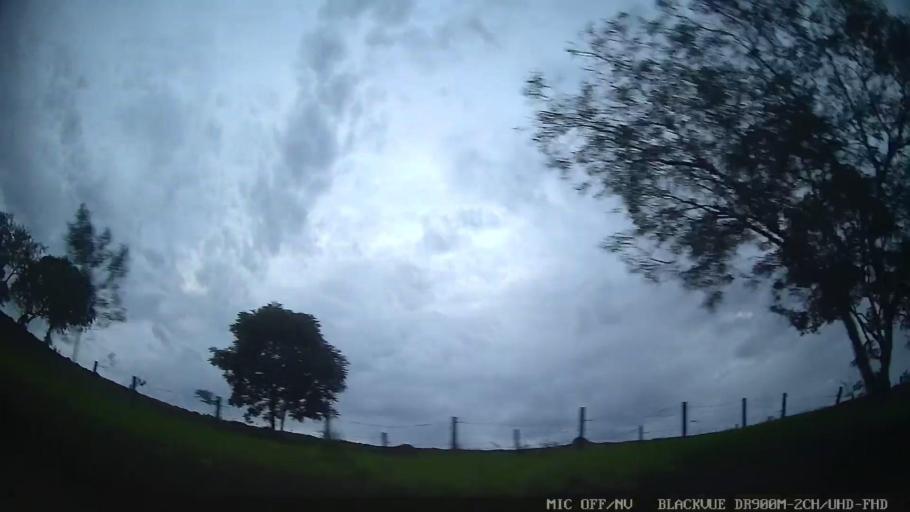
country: BR
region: Sao Paulo
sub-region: Amparo
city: Amparo
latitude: -22.8552
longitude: -46.7844
